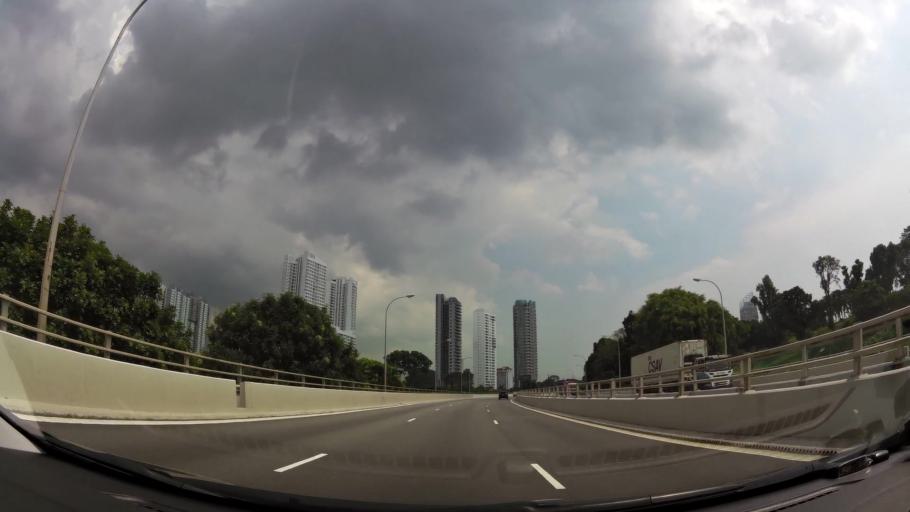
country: SG
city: Singapore
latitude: 1.2728
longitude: 103.8033
